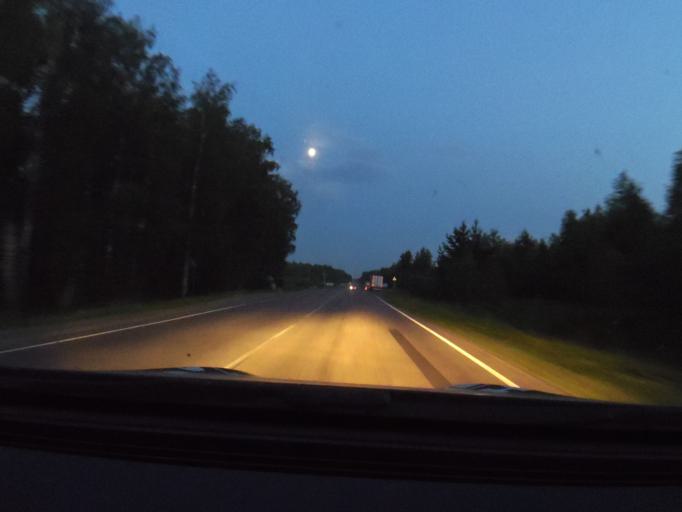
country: RU
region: Bashkortostan
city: Duvan
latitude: 56.0064
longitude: 58.2130
